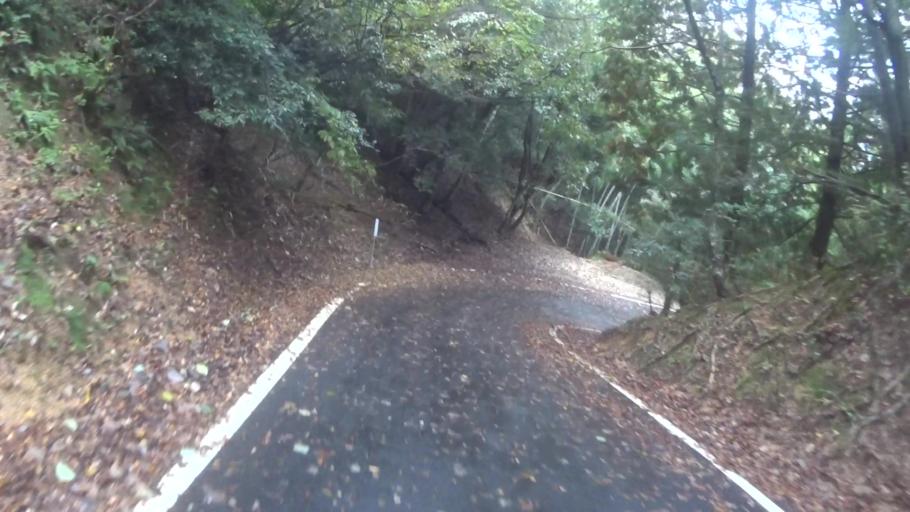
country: JP
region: Kyoto
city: Miyazu
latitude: 35.5009
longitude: 135.0411
